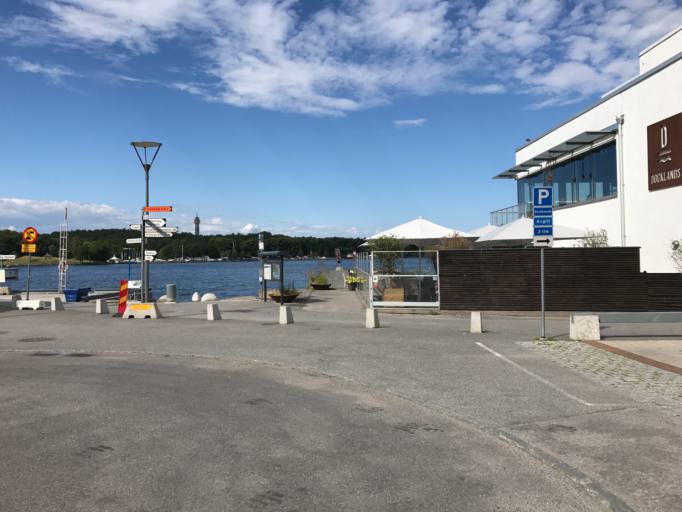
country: SE
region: Stockholm
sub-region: Nacka Kommun
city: Nacka
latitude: 59.3158
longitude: 18.1243
